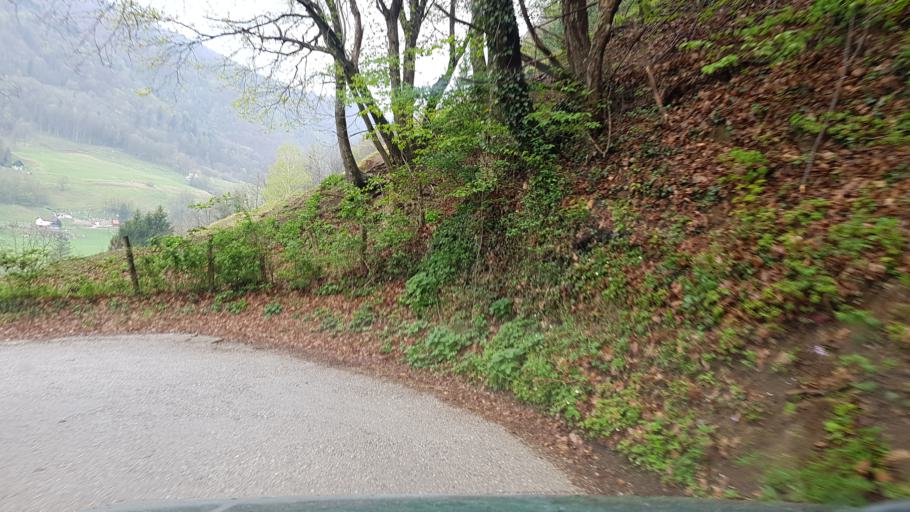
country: SI
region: Tolmin
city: Tolmin
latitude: 46.1426
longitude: 13.7778
